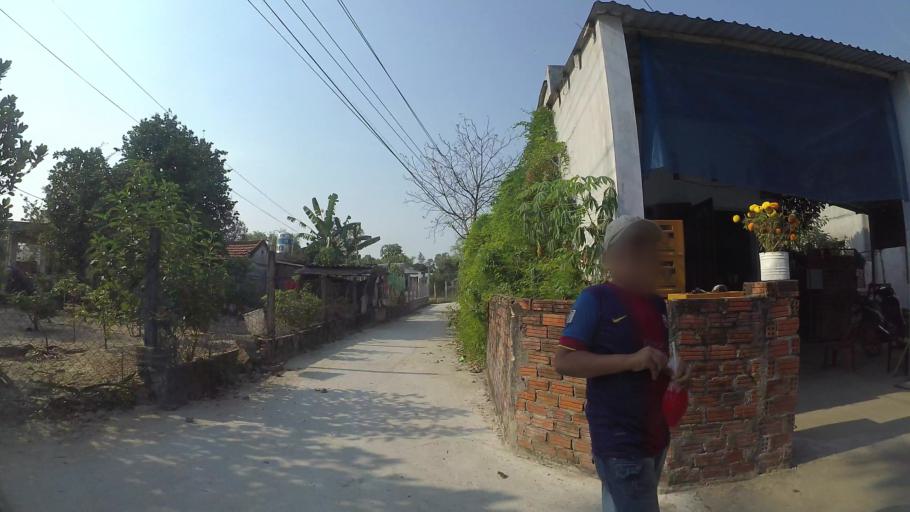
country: VN
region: Quang Nam
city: Quang Nam
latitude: 15.9475
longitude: 108.2575
